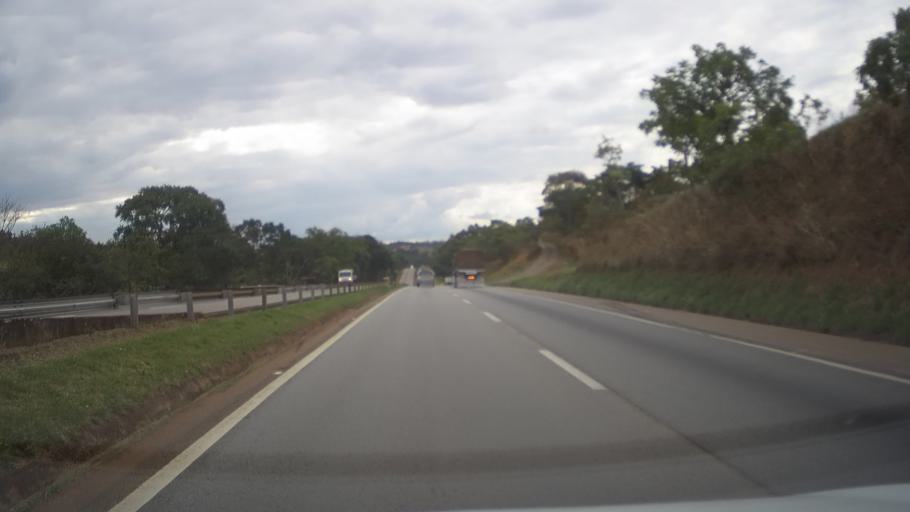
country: BR
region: Minas Gerais
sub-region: Itauna
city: Itauna
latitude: -20.3343
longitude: -44.4482
